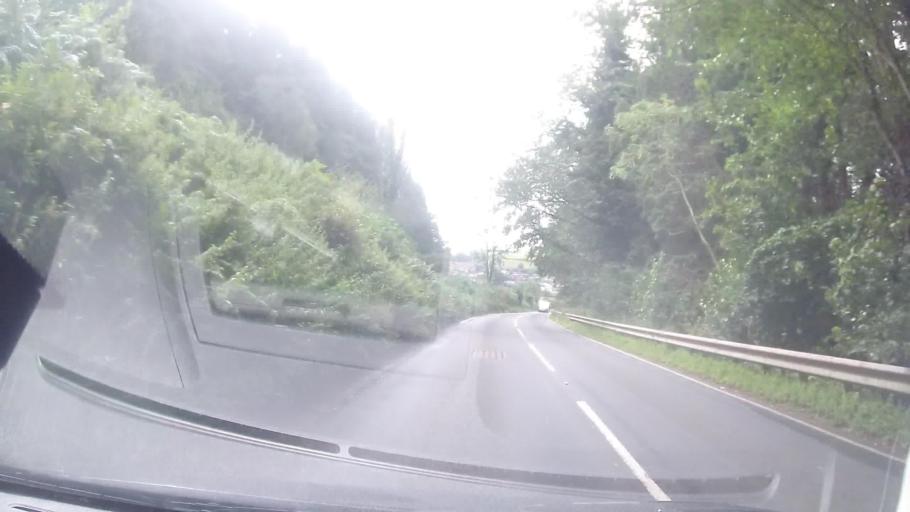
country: GB
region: Wales
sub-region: Sir Powys
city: Knighton
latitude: 52.3444
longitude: -3.0286
